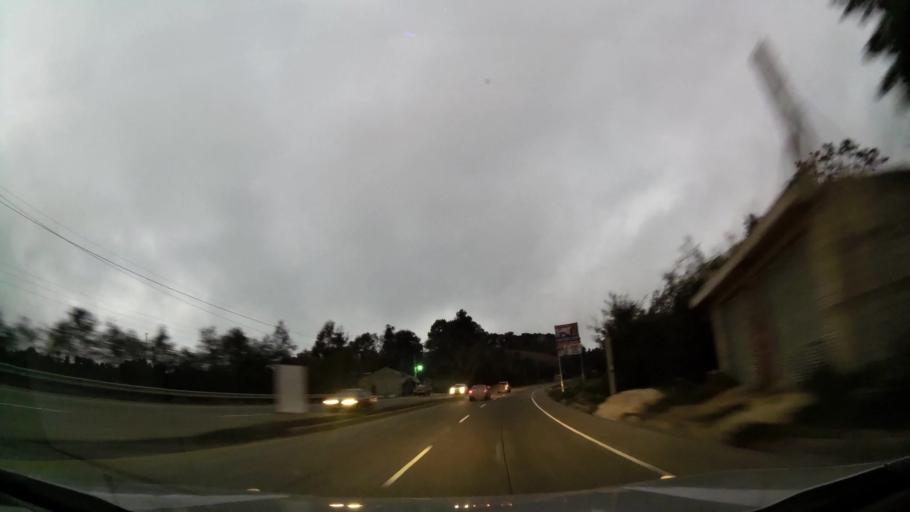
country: GT
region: Chimaltenango
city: Santa Apolonia
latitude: 14.8272
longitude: -91.0161
